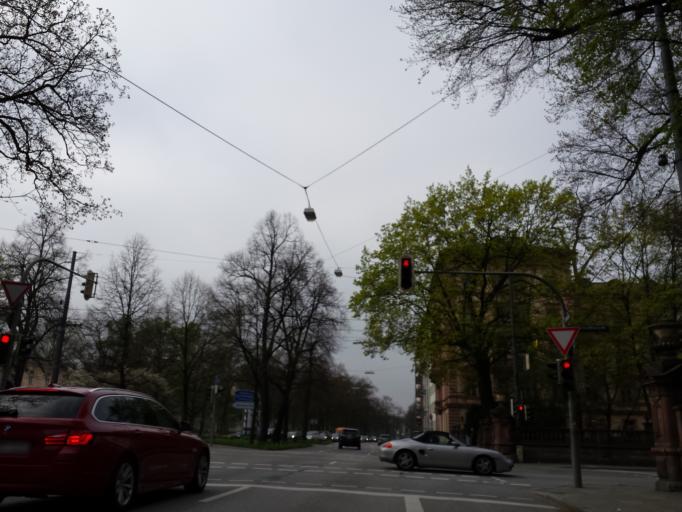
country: DE
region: Bavaria
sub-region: Upper Bavaria
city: Munich
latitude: 48.1376
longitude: 11.5892
